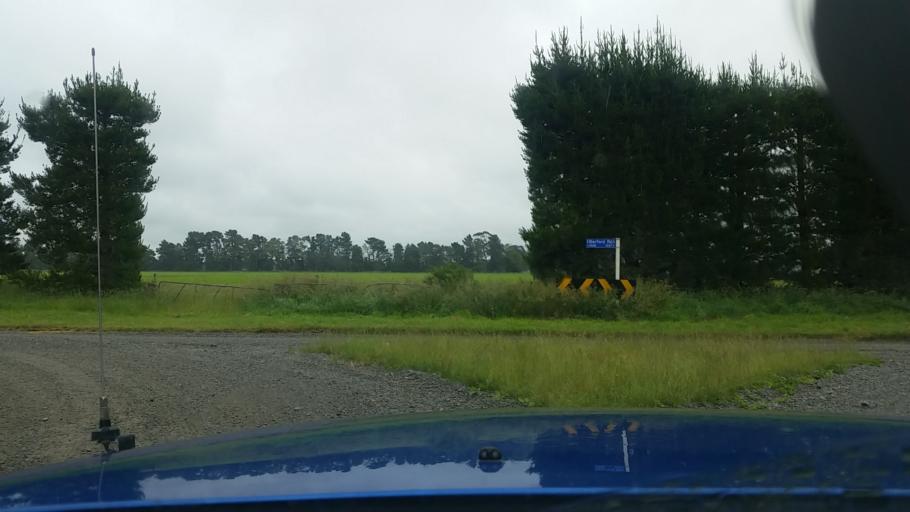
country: NZ
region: Canterbury
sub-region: Ashburton District
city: Tinwald
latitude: -43.9094
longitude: 171.5443
